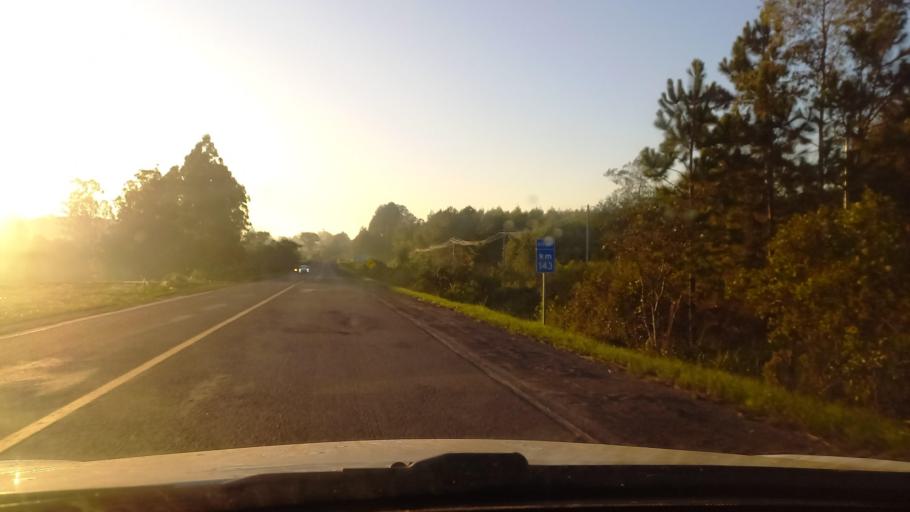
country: BR
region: Rio Grande do Sul
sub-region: Candelaria
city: Candelaria
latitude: -29.6807
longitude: -52.8265
